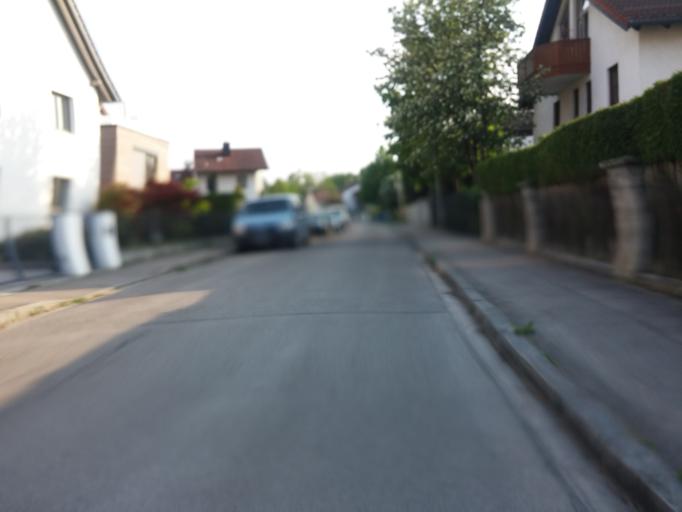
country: DE
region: Bavaria
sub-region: Upper Bavaria
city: Neubiberg
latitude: 48.1283
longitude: 11.6719
